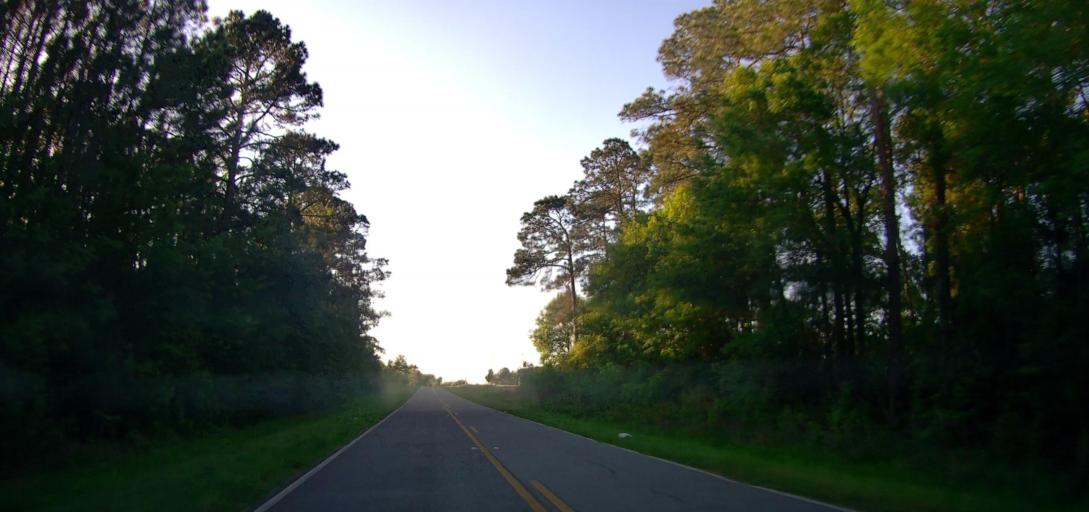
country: US
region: Georgia
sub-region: Ben Hill County
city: Fitzgerald
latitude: 31.6907
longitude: -83.2327
